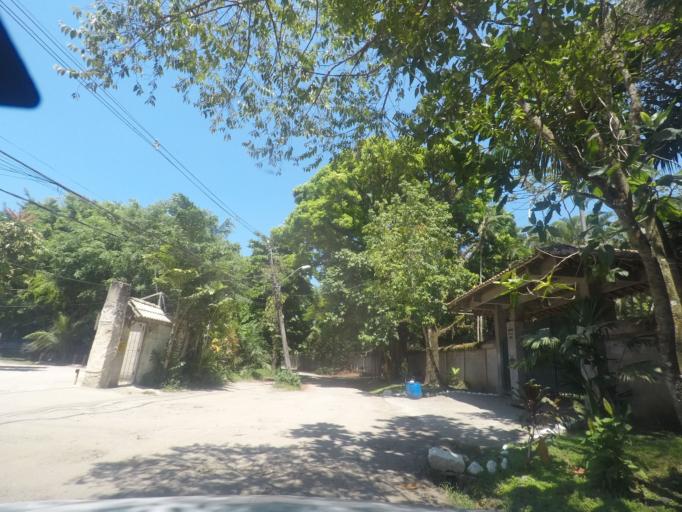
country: BR
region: Rio de Janeiro
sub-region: Nilopolis
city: Nilopolis
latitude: -22.9776
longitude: -43.4518
